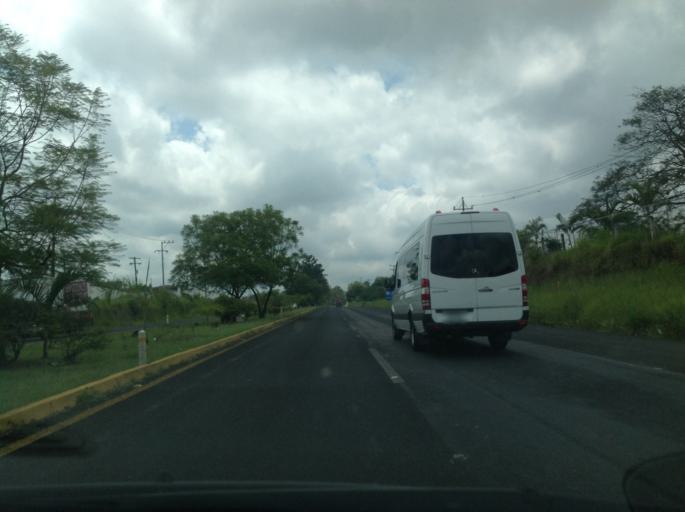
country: MX
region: Veracruz
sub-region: Emiliano Zapata
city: Jacarandas
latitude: 19.5035
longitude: -96.8469
